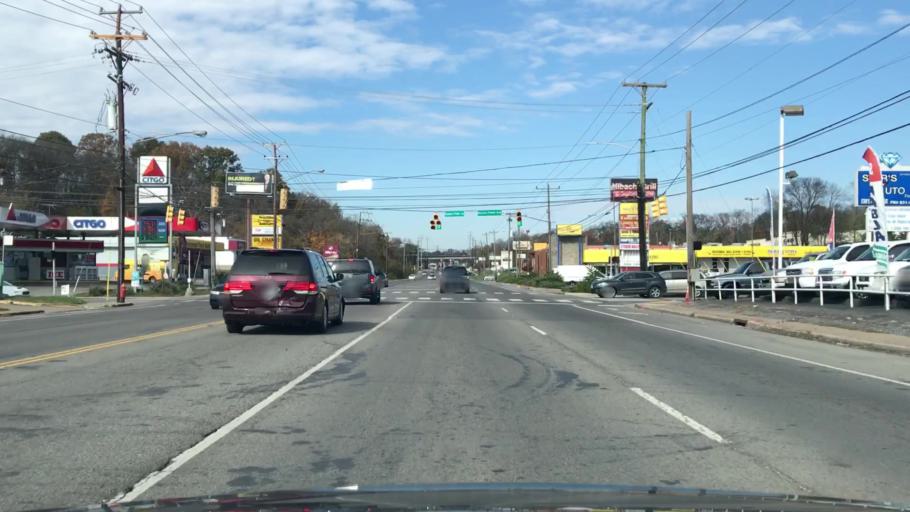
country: US
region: Tennessee
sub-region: Davidson County
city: Oak Hill
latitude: 36.0866
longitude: -86.7298
